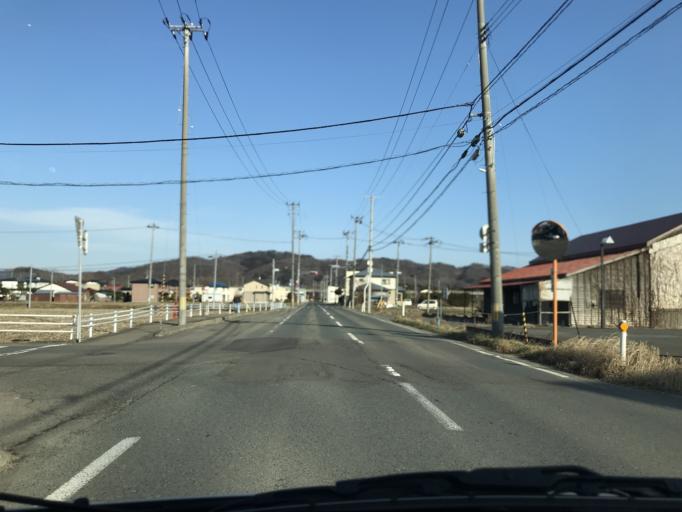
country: JP
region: Iwate
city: Kitakami
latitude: 39.2720
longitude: 141.1109
